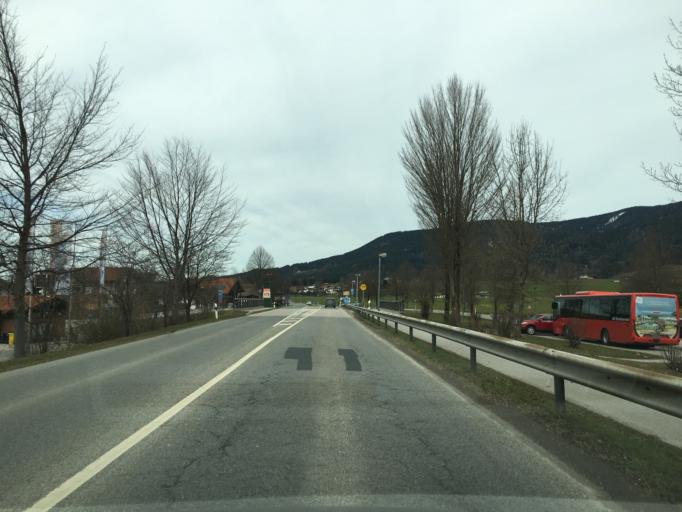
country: DE
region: Bavaria
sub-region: Upper Bavaria
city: Inzell
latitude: 47.7651
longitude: 12.7479
